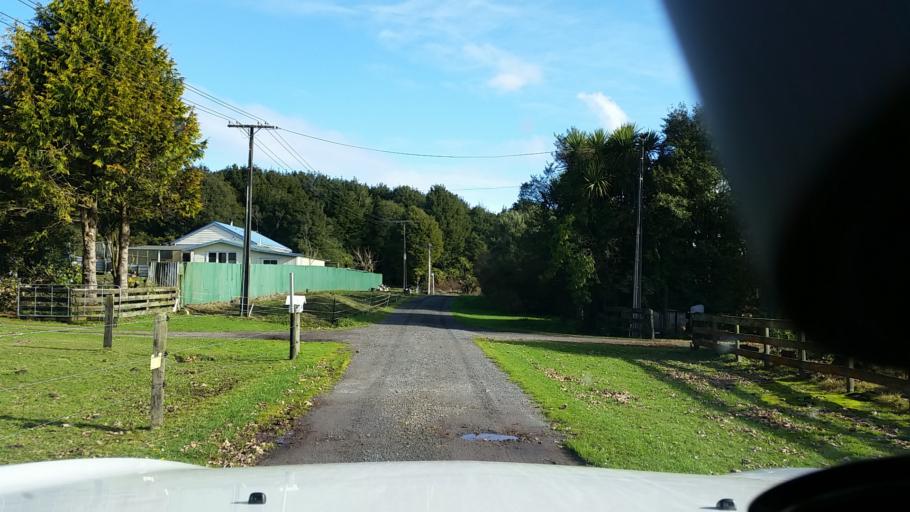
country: NZ
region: Bay of Plenty
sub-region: Rotorua District
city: Rotorua
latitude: -38.0916
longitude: 176.0739
